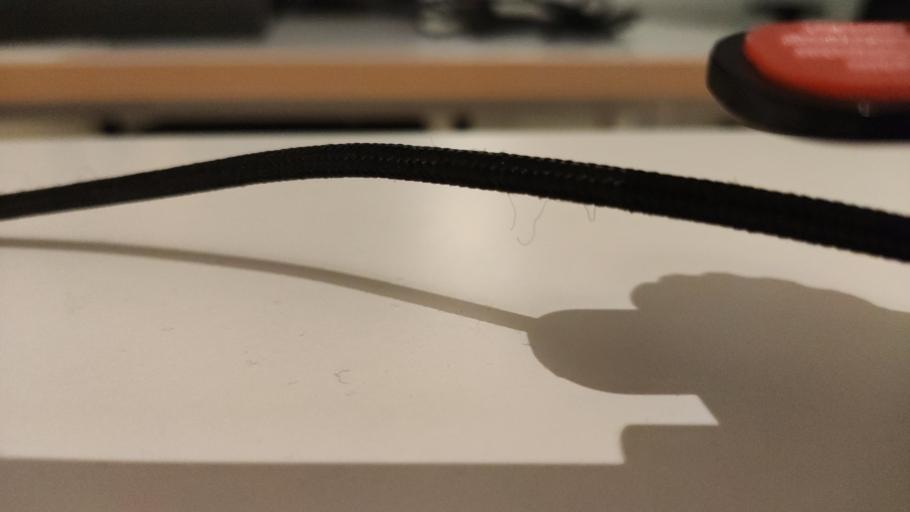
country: RU
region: Moskovskaya
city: Kurovskoye
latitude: 55.5801
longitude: 38.8890
